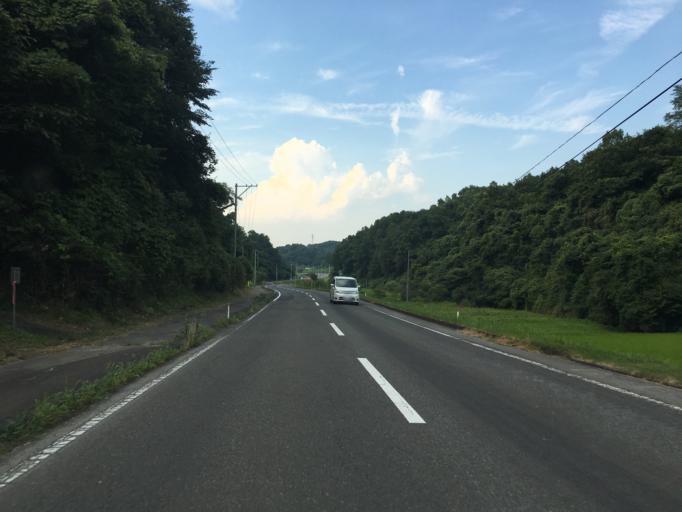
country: JP
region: Fukushima
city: Nihommatsu
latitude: 37.5414
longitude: 140.4417
